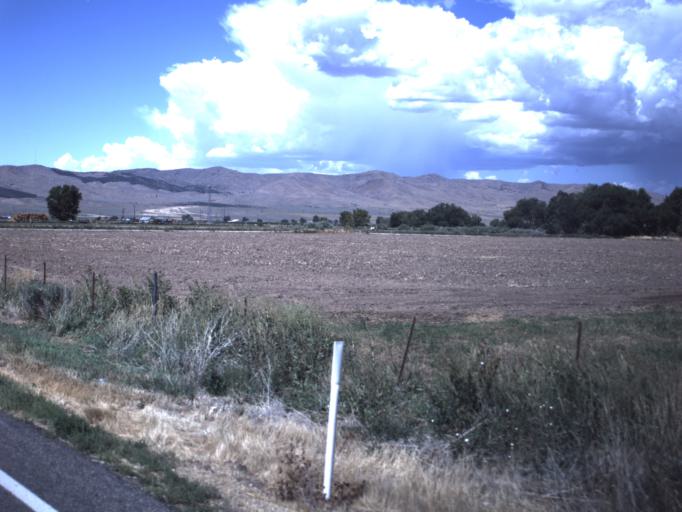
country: US
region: Utah
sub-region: Juab County
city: Nephi
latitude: 39.7100
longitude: -111.8574
